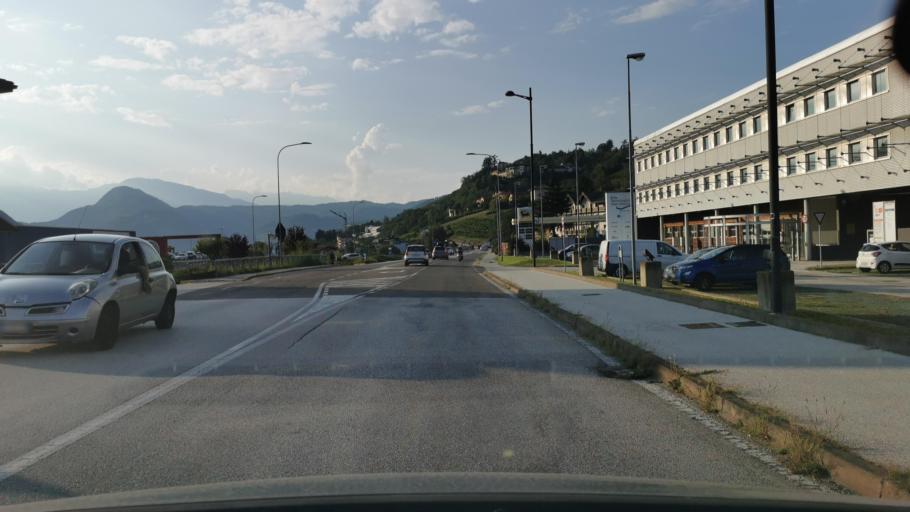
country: IT
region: Trentino-Alto Adige
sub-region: Provincia di Trento
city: Pergine Valsugana
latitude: 46.0675
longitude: 11.2259
